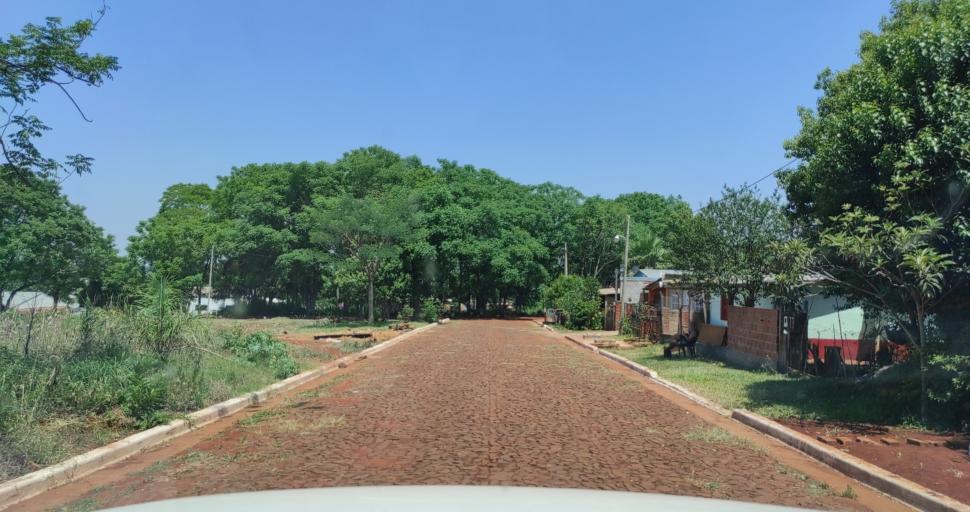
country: AR
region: Misiones
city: Santo Pipo
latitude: -27.1081
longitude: -55.3425
